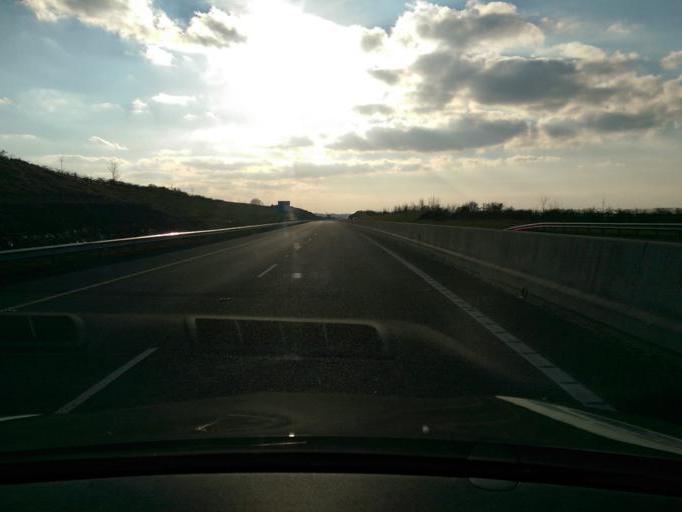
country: IE
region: Leinster
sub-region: Laois
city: Rathdowney
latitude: 52.9267
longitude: -7.5984
